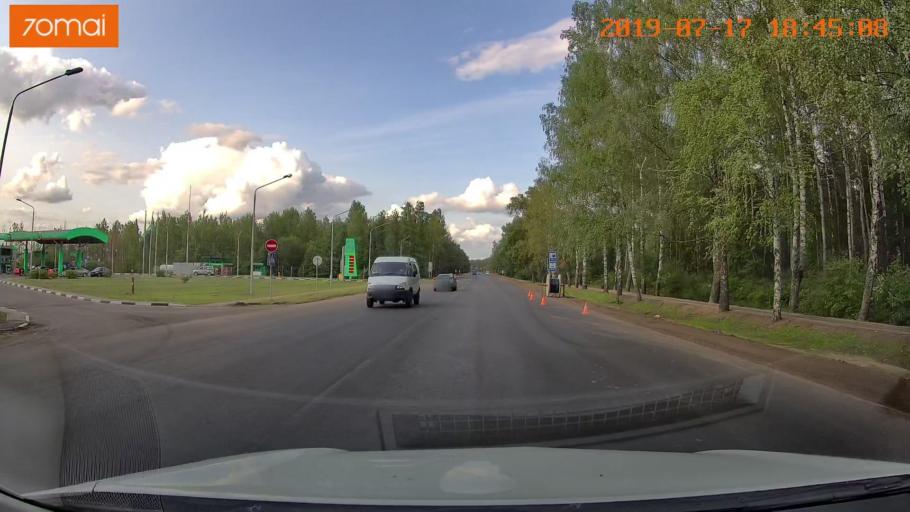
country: BY
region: Mogilev
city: Asipovichy
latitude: 53.3226
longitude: 28.6516
